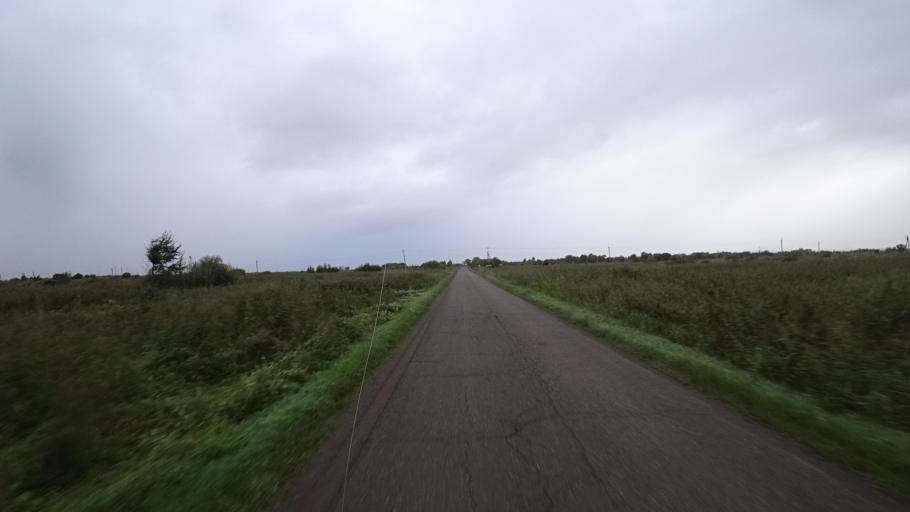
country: RU
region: Primorskiy
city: Chernigovka
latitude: 44.3930
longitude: 132.5286
